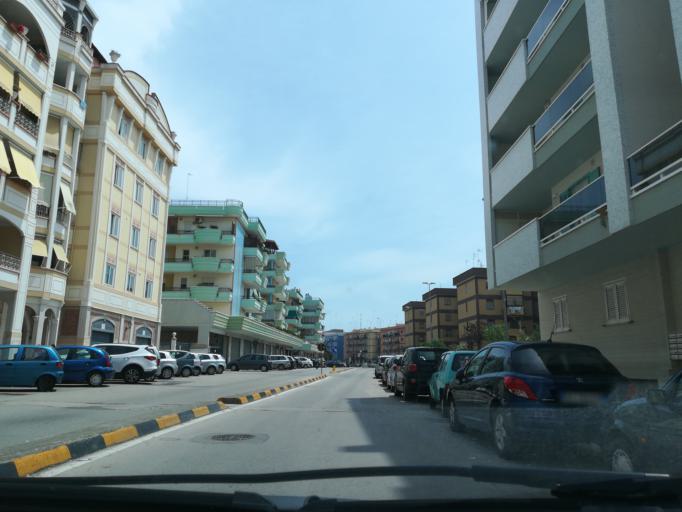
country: IT
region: Apulia
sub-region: Provincia di Barletta - Andria - Trani
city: Barletta
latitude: 41.3234
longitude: 16.2672
